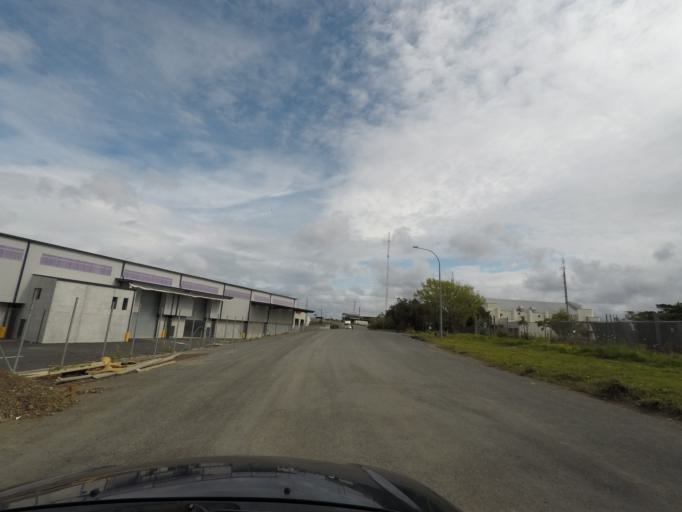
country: NZ
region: Auckland
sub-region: Auckland
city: Rosebank
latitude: -36.8446
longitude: 174.6321
